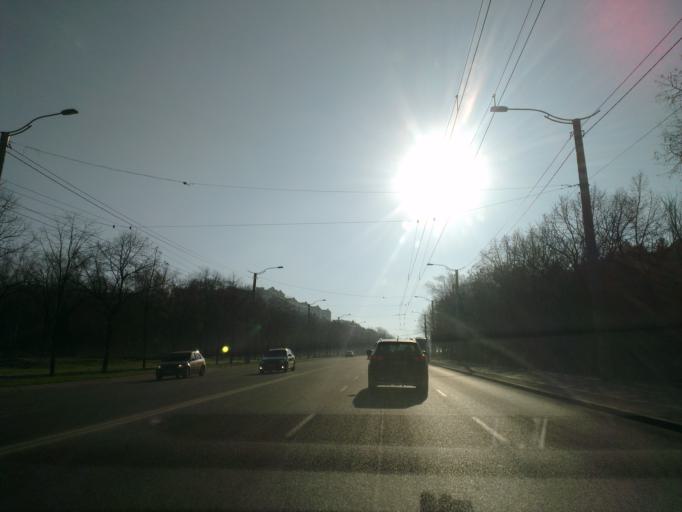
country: MD
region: Chisinau
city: Chisinau
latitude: 47.0418
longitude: 28.8744
